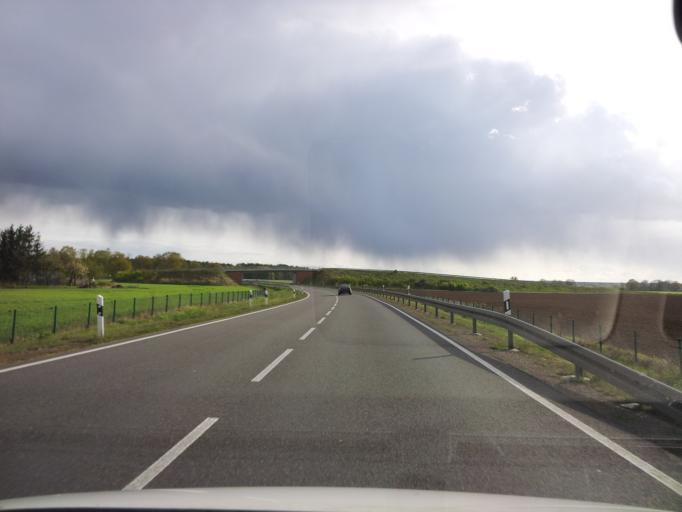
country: DE
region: Brandenburg
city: Guben
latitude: 51.8997
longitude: 14.6781
